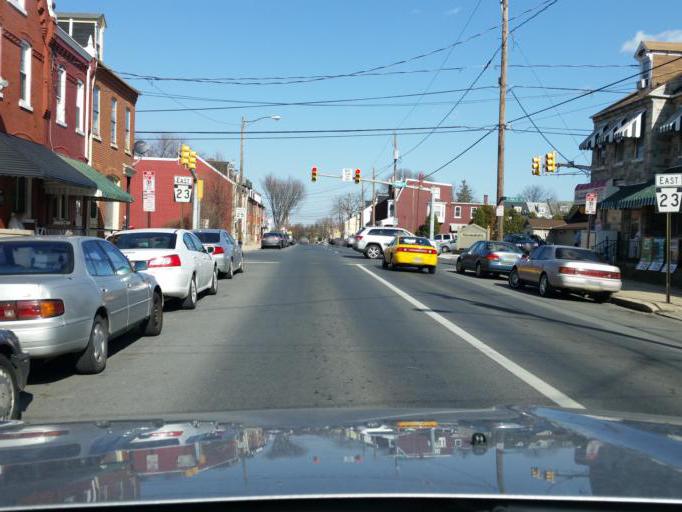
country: US
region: Pennsylvania
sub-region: Lancaster County
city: Lancaster
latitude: 40.0426
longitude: -76.2923
